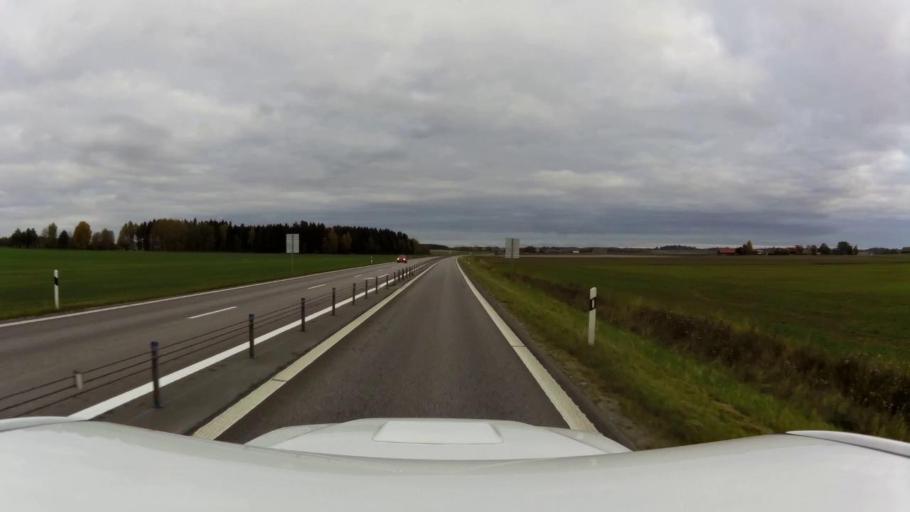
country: SE
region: OEstergoetland
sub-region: Linkopings Kommun
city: Berg
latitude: 58.4555
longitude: 15.5017
